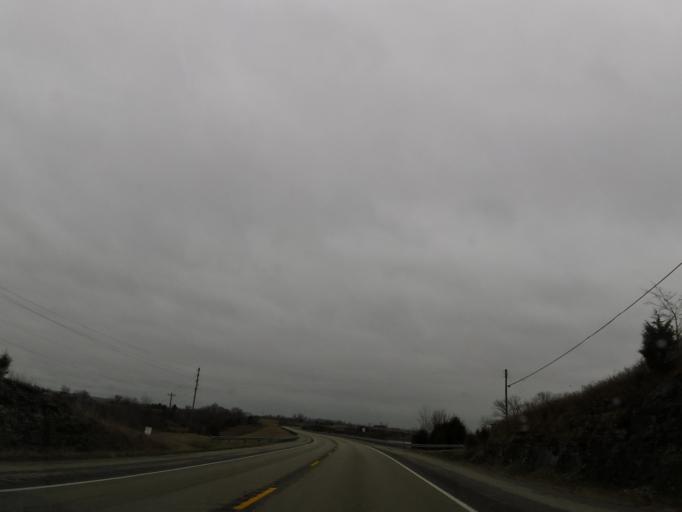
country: US
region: Kentucky
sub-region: Lincoln County
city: Stanford
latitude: 37.4961
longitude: -84.5546
